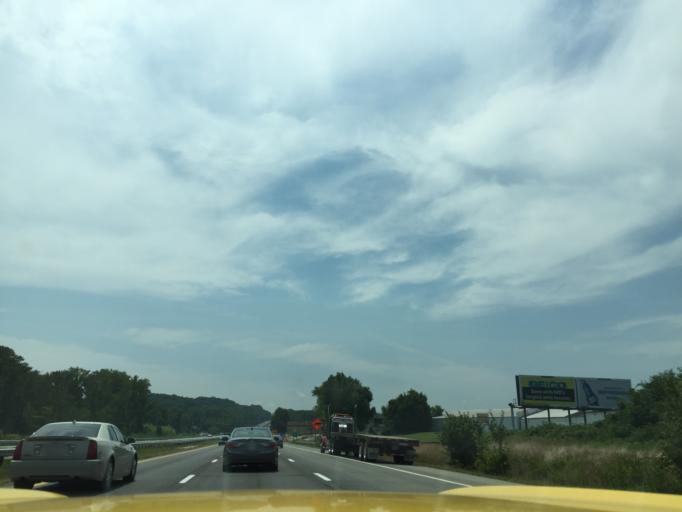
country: US
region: Maryland
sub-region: Prince George's County
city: Friendly
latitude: 38.7313
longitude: -76.9907
